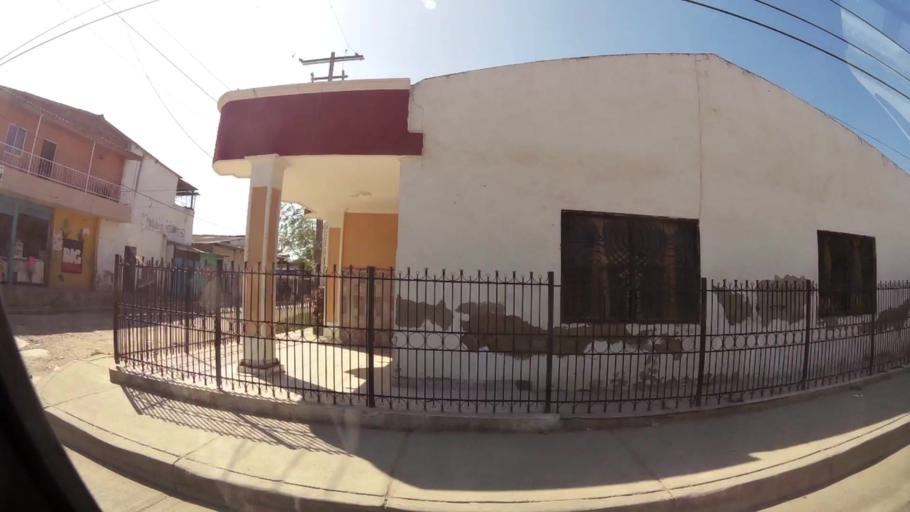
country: CO
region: Bolivar
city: Cartagena
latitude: 10.4127
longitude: -75.5119
